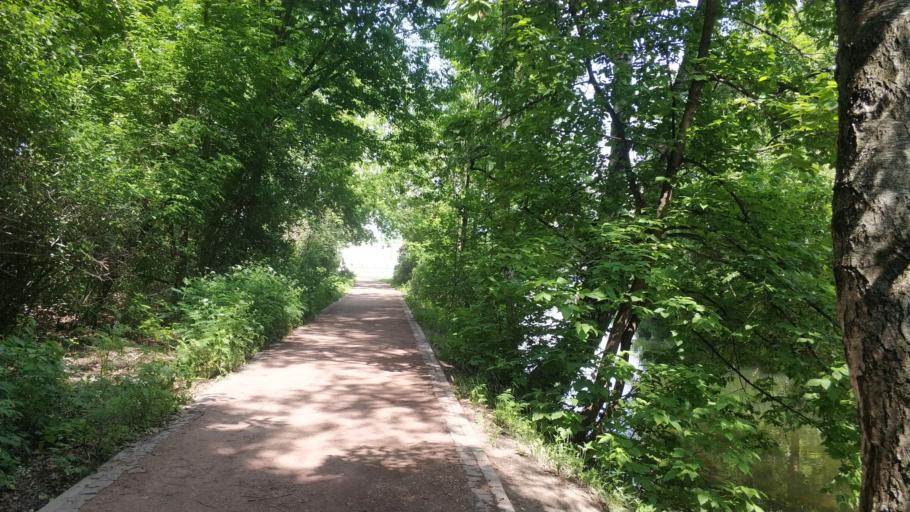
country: RU
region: Moscow
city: Perovo
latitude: 55.7327
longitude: 37.8049
